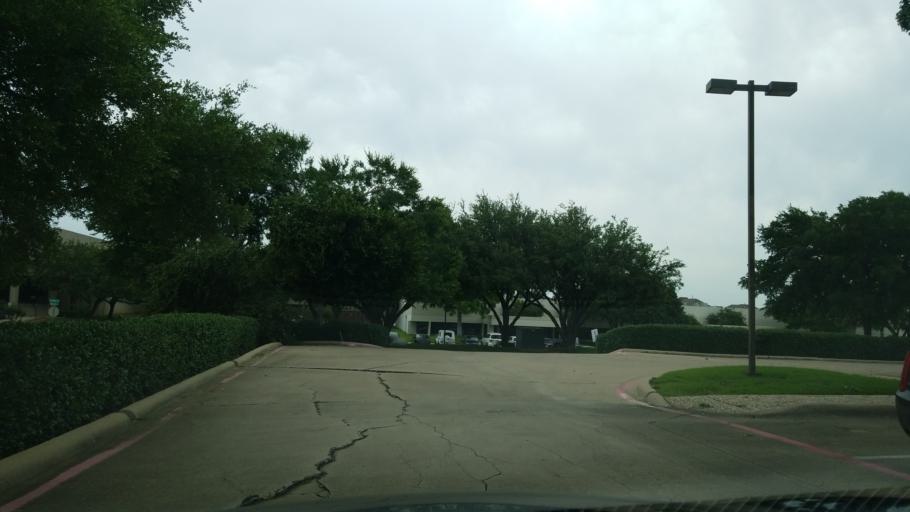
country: US
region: Texas
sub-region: Dallas County
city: Coppell
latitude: 32.8970
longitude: -96.9865
